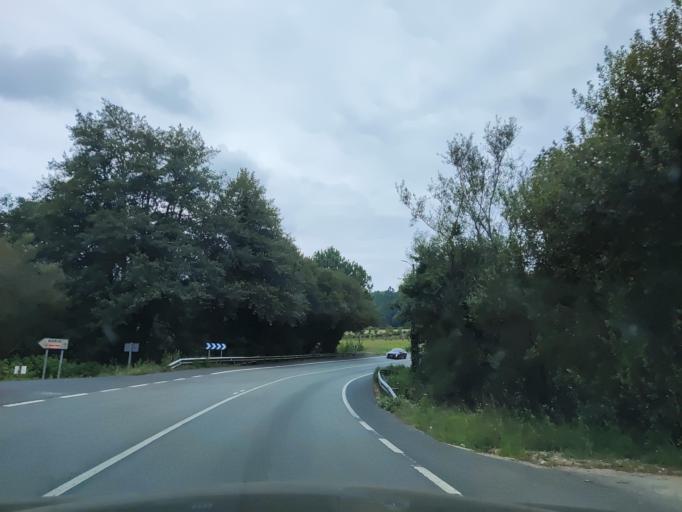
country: ES
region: Galicia
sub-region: Provincia da Coruna
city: Teo
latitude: 42.7783
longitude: -8.5519
